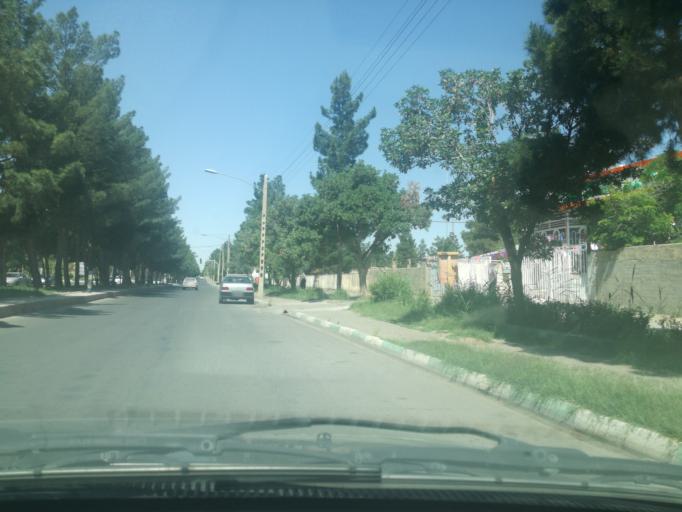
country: IR
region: Razavi Khorasan
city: Sarakhs
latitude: 36.5373
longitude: 61.1576
